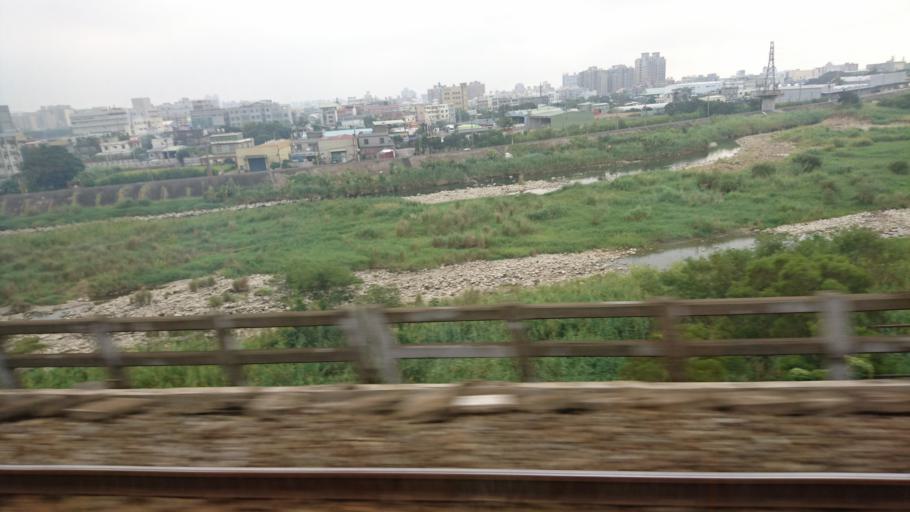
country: TW
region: Taiwan
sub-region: Hsinchu
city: Zhubei
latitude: 24.8532
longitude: 121.0115
